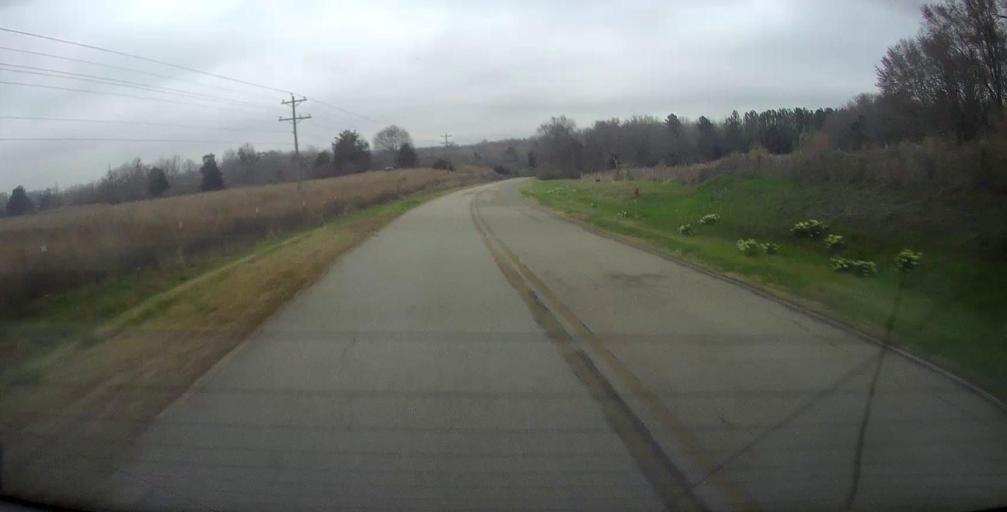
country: US
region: Georgia
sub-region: Lamar County
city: Barnesville
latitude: 33.0396
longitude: -84.1122
